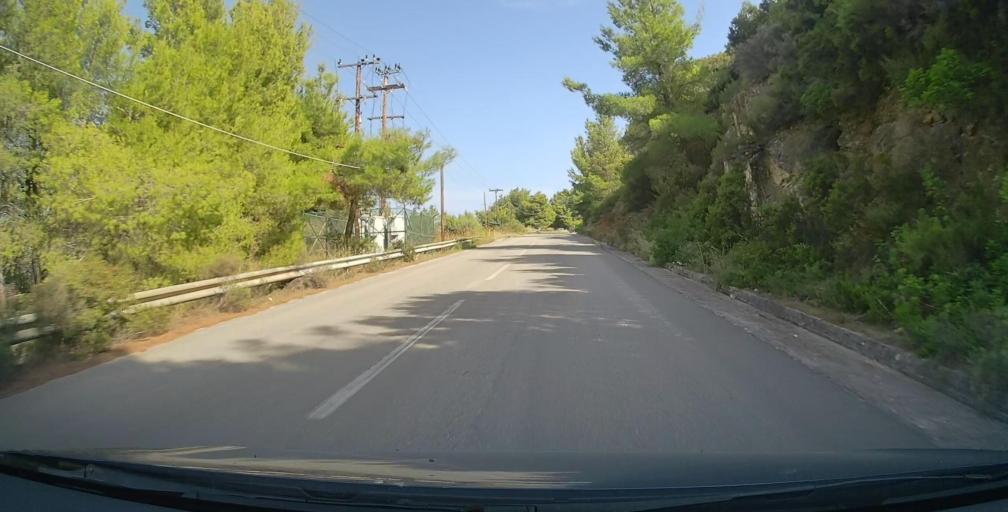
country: GR
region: Central Macedonia
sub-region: Nomos Chalkidikis
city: Sarti
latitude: 40.1132
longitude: 23.9854
